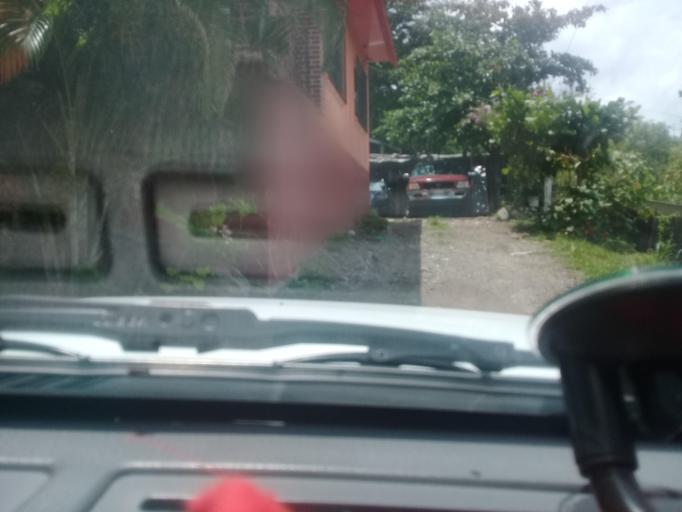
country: MX
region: Veracruz
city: Paso de Ovejas
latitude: 19.2819
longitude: -96.4292
